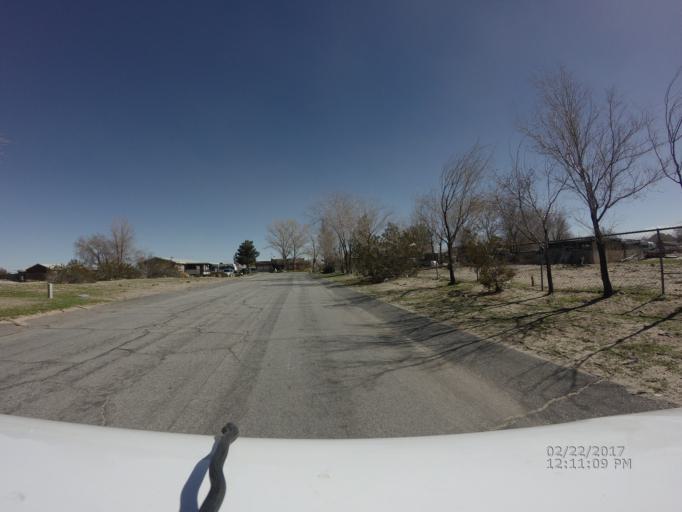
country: US
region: California
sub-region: Los Angeles County
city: Lake Los Angeles
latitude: 34.6228
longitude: -117.8293
